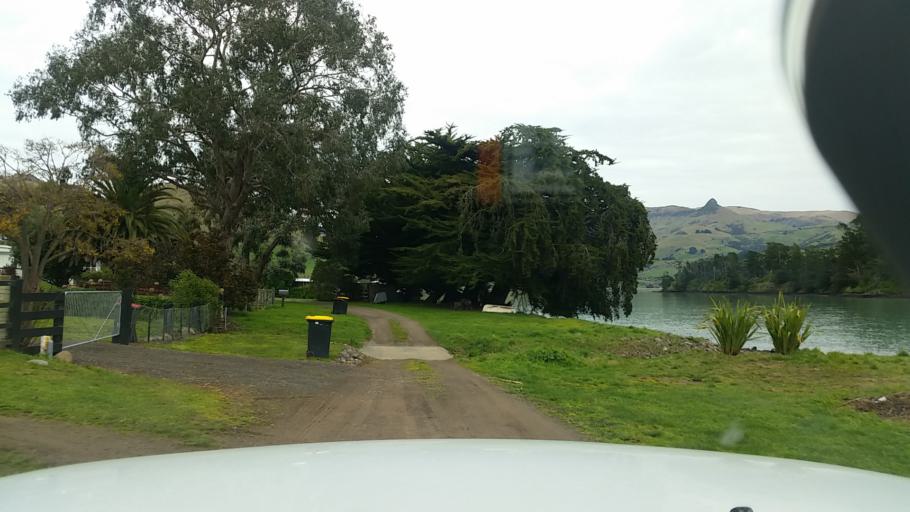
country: NZ
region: Canterbury
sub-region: Christchurch City
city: Christchurch
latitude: -43.6482
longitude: 172.8364
